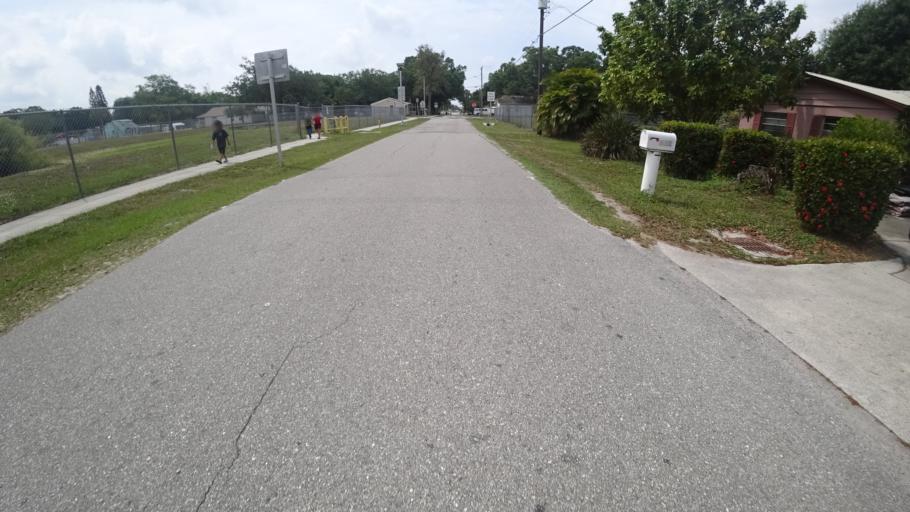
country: US
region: Florida
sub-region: Manatee County
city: Samoset
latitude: 27.4702
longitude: -82.5441
